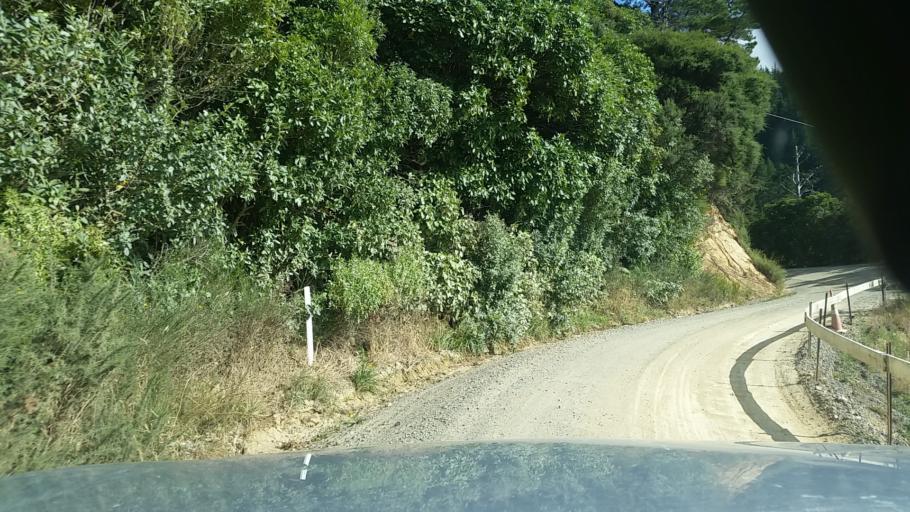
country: NZ
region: Marlborough
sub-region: Marlborough District
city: Picton
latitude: -41.2919
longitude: 174.1299
